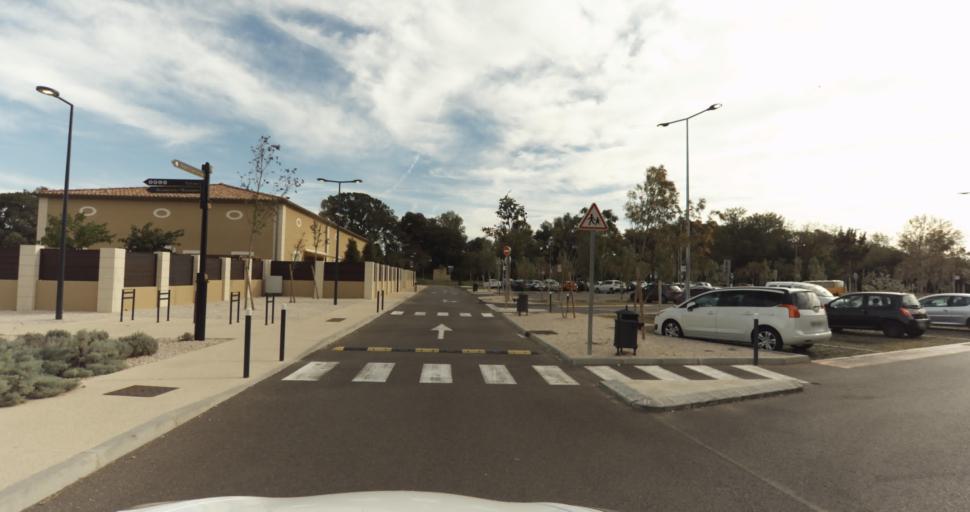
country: FR
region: Provence-Alpes-Cote d'Azur
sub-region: Departement des Bouches-du-Rhone
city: Miramas
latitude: 43.5938
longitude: 4.9952
